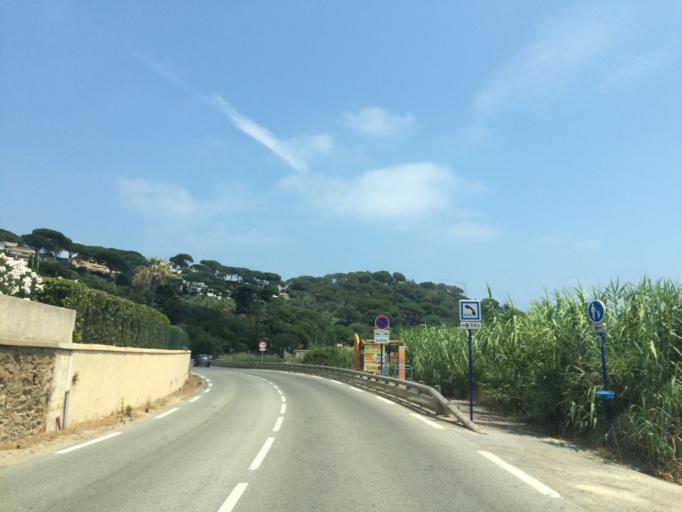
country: FR
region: Provence-Alpes-Cote d'Azur
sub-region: Departement du Var
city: Sainte-Maxime
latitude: 43.3135
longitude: 6.6578
